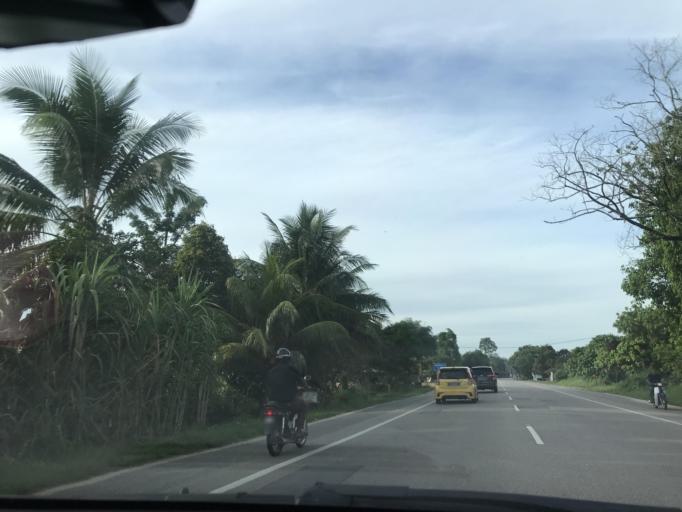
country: MY
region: Kelantan
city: Ketereh
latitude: 5.9738
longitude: 102.1923
